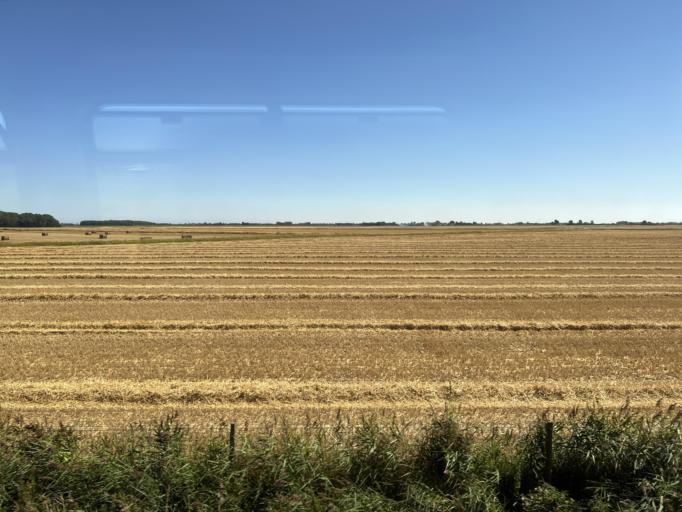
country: GB
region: England
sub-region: Lincolnshire
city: Spilsby
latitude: 53.1043
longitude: 0.1158
